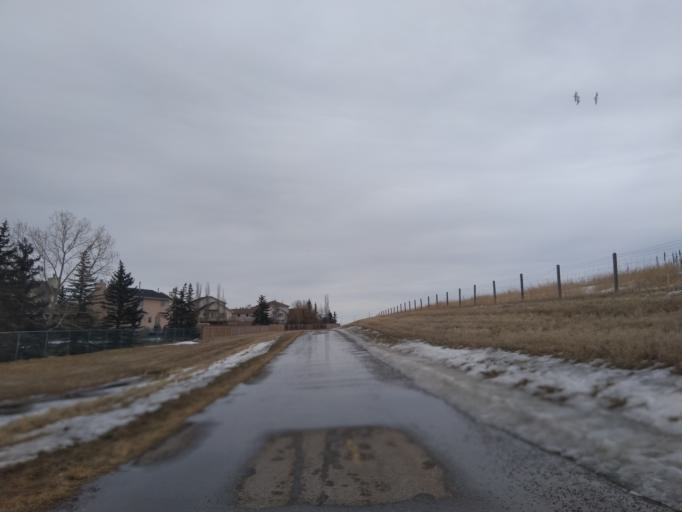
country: CA
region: Alberta
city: Chestermere
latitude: 51.0969
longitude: -113.9318
